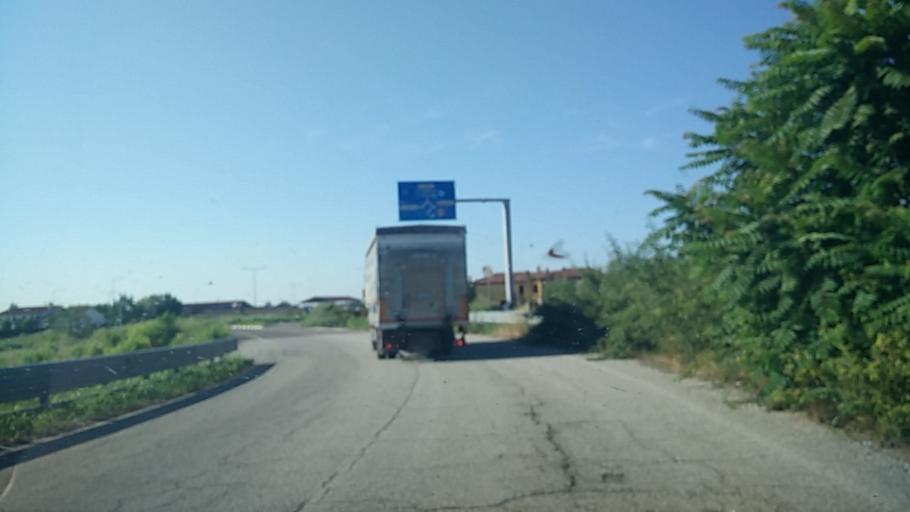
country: IT
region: Veneto
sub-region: Provincia di Venezia
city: Cazzago-Ex Polo
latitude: 45.4446
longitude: 12.0897
